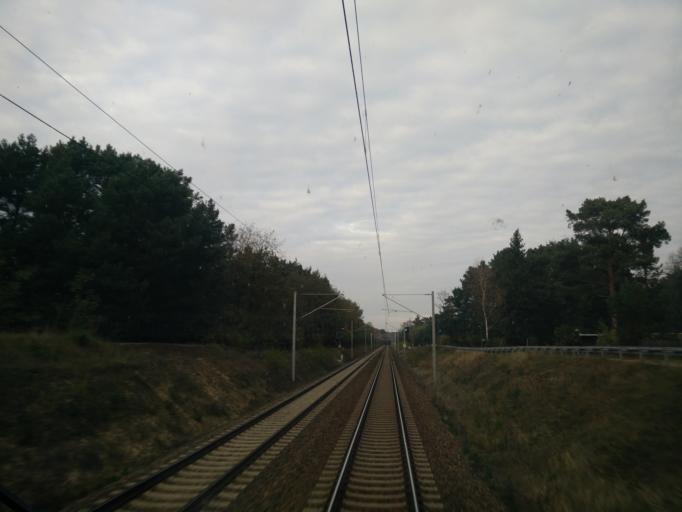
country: DE
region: Brandenburg
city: Bestensee
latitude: 52.2182
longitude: 13.6197
